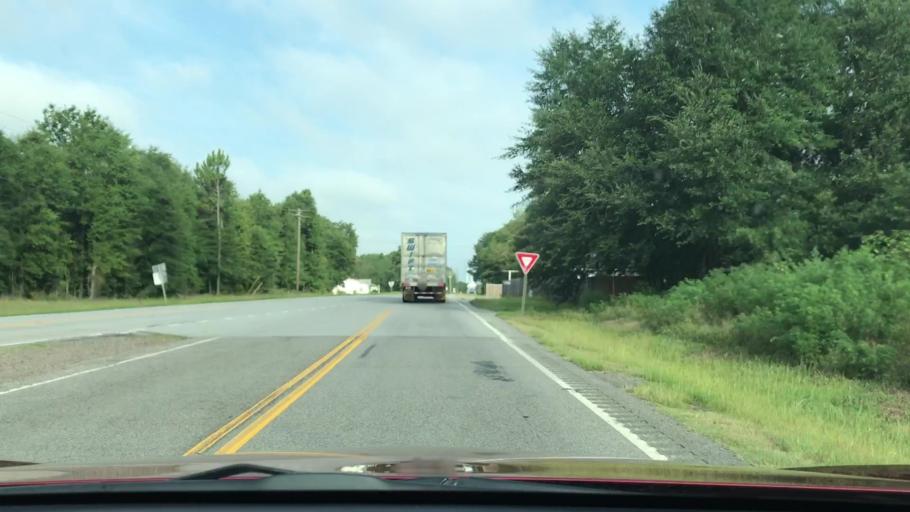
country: US
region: South Carolina
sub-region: Barnwell County
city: Williston
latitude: 33.6345
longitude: -81.3177
